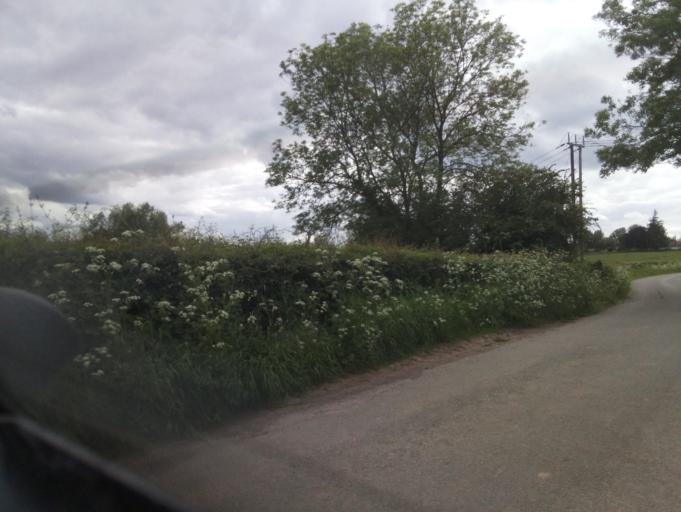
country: GB
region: England
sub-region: Herefordshire
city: Ledbury
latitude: 52.0341
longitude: -2.4648
